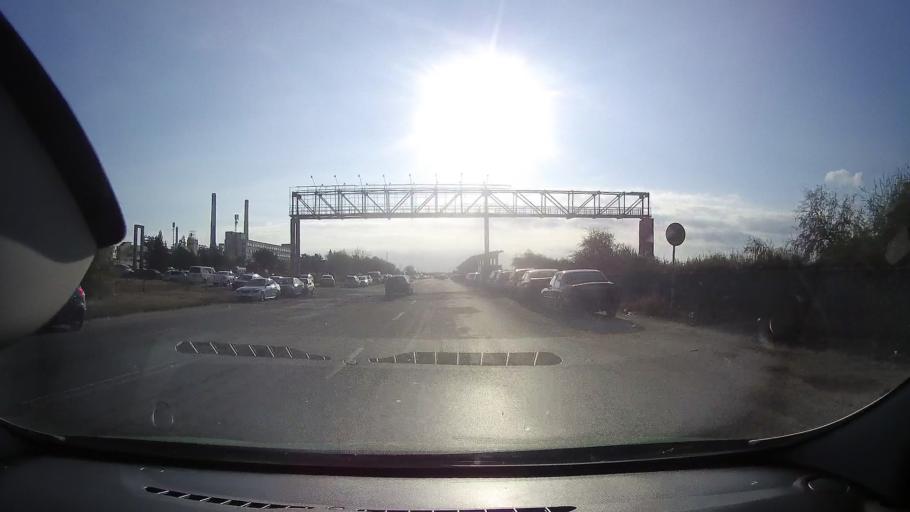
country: RO
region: Constanta
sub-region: Comuna Corbu
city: Corbu
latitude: 44.3466
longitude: 28.6439
